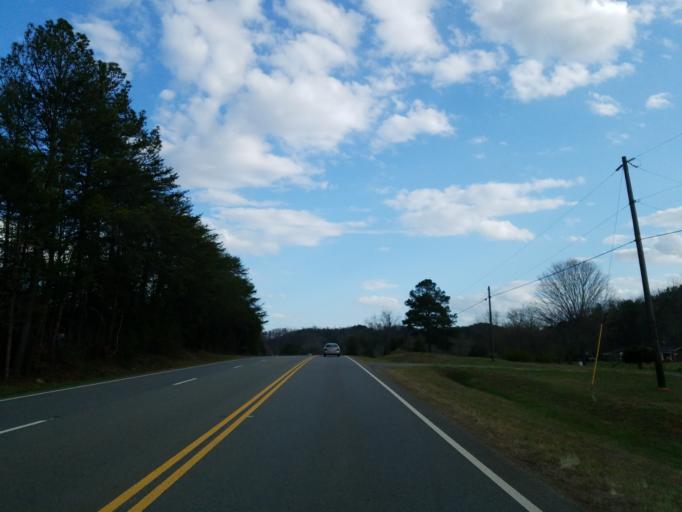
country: US
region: Georgia
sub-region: Bartow County
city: Rydal
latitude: 34.4416
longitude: -84.7224
